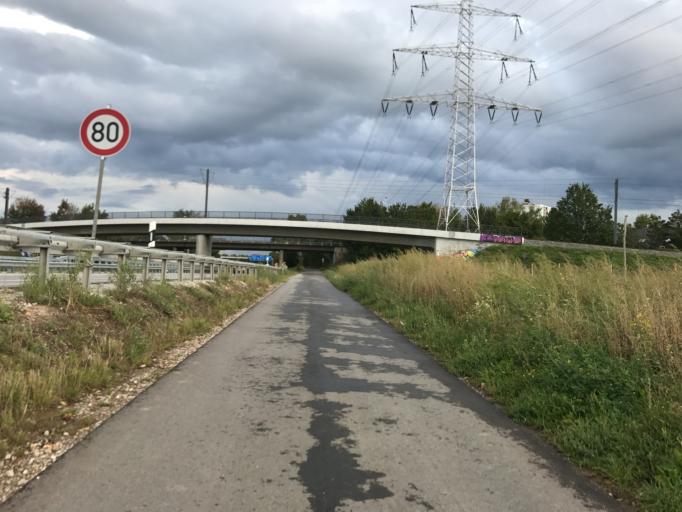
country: DE
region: Rheinland-Pfalz
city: Klein-Winternheim
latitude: 49.9652
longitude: 8.2299
